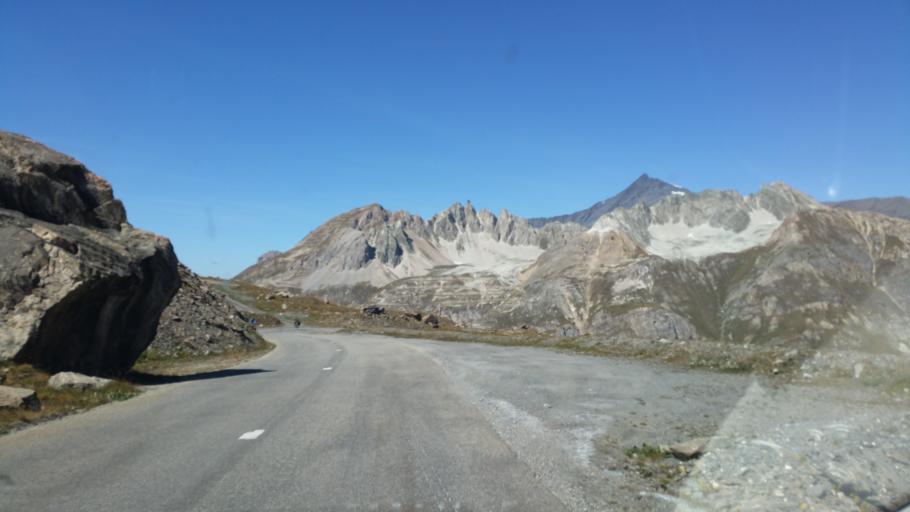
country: FR
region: Rhone-Alpes
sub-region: Departement de la Savoie
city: Val-d'Isere
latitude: 45.4346
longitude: 7.0147
